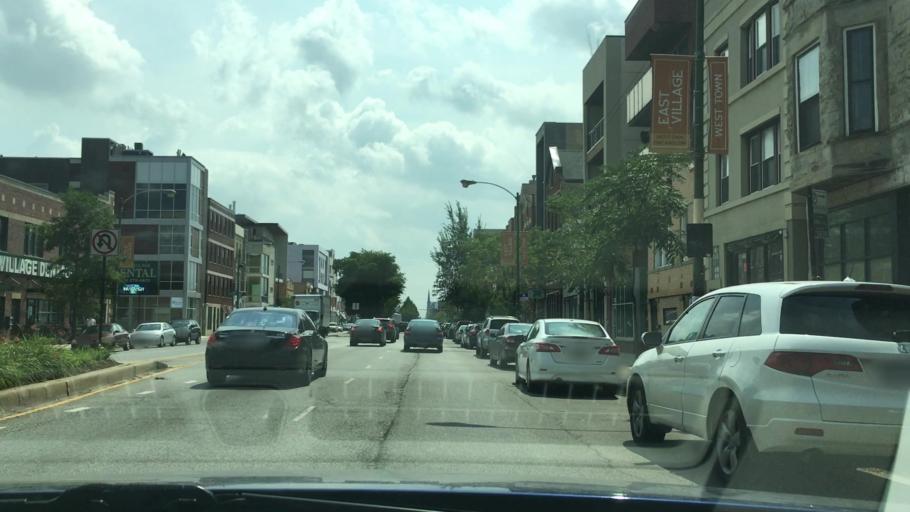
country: US
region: Illinois
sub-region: Cook County
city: Chicago
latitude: 41.8985
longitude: -87.6674
